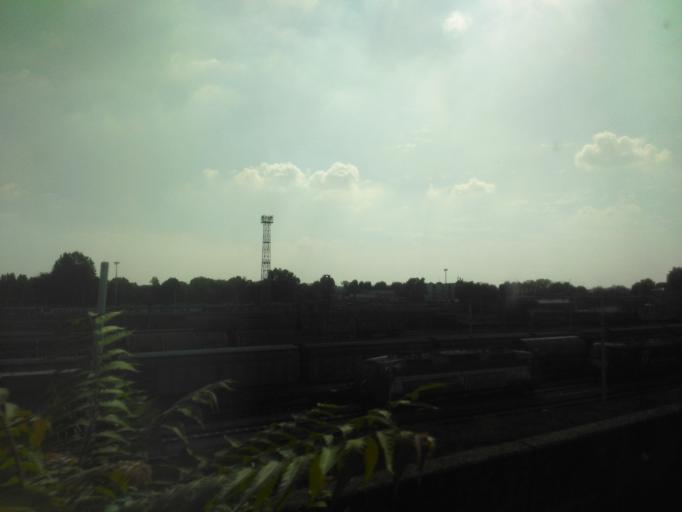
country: IT
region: Lombardy
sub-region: Citta metropolitana di Milano
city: Novegro-Tregarezzo-San Felice
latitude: 45.4742
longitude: 9.2632
